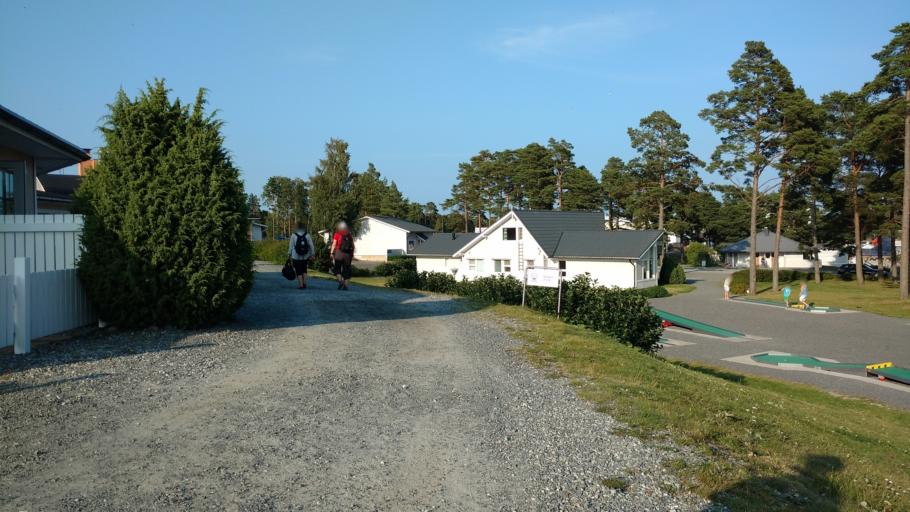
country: FI
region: Varsinais-Suomi
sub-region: Aboland-Turunmaa
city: Dragsfjaerd
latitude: 59.9214
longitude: 22.4077
